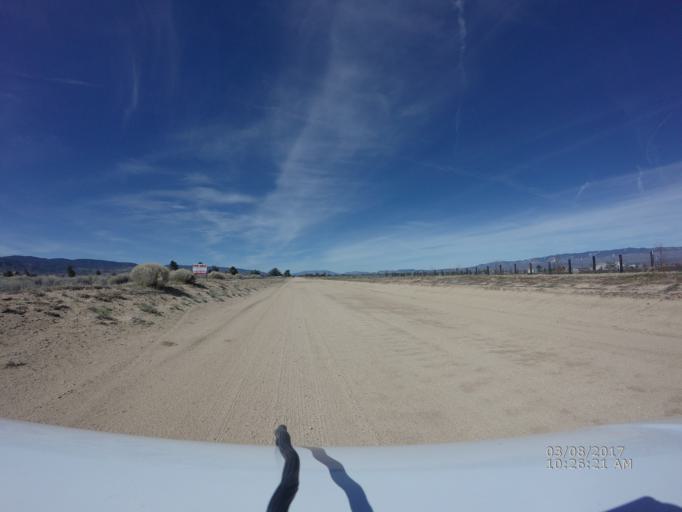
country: US
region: California
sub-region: Los Angeles County
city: Green Valley
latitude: 34.7602
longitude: -118.4602
